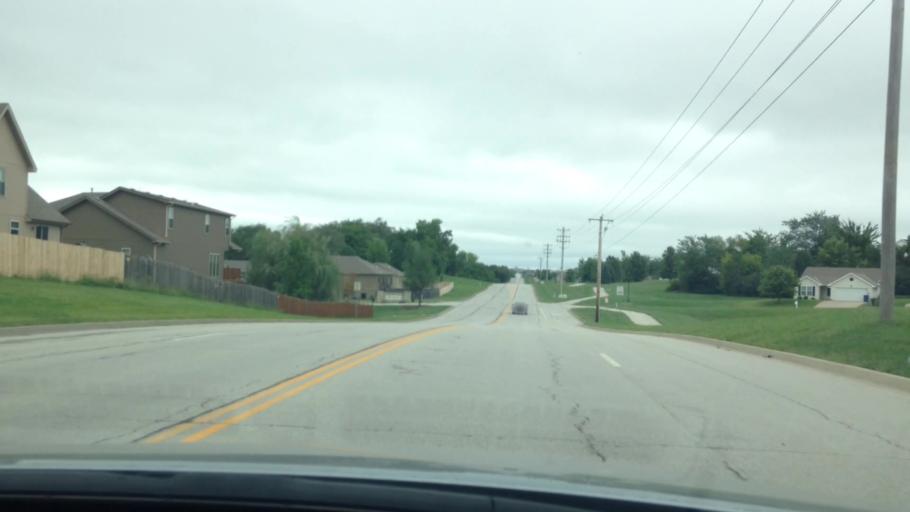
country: US
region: Missouri
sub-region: Platte County
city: Platte City
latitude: 39.3185
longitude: -94.7611
